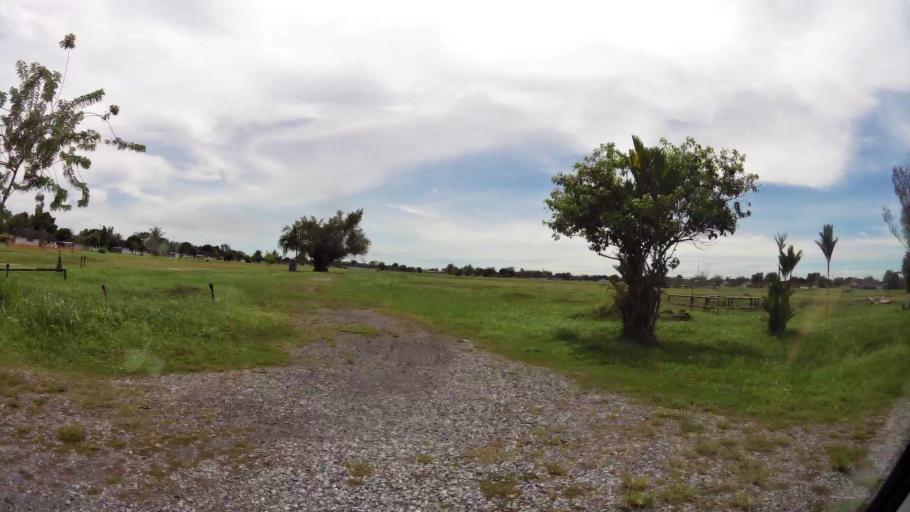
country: BN
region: Belait
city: Seria
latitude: 4.6063
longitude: 114.3167
